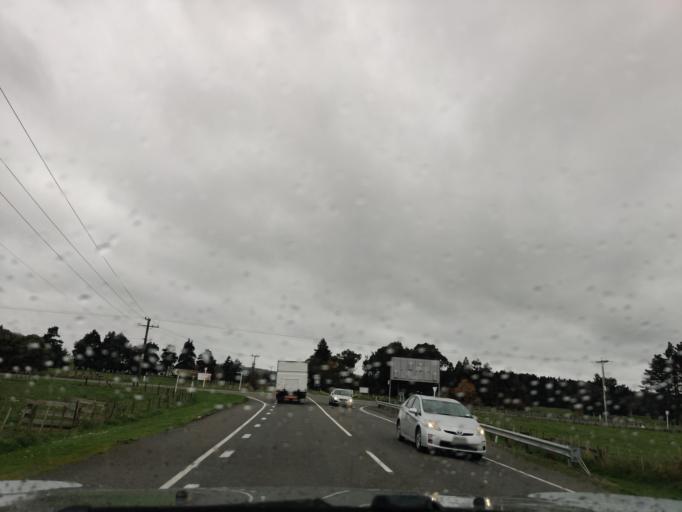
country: NZ
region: Manawatu-Wanganui
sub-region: Palmerston North City
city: Palmerston North
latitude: -40.3403
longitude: 175.8790
